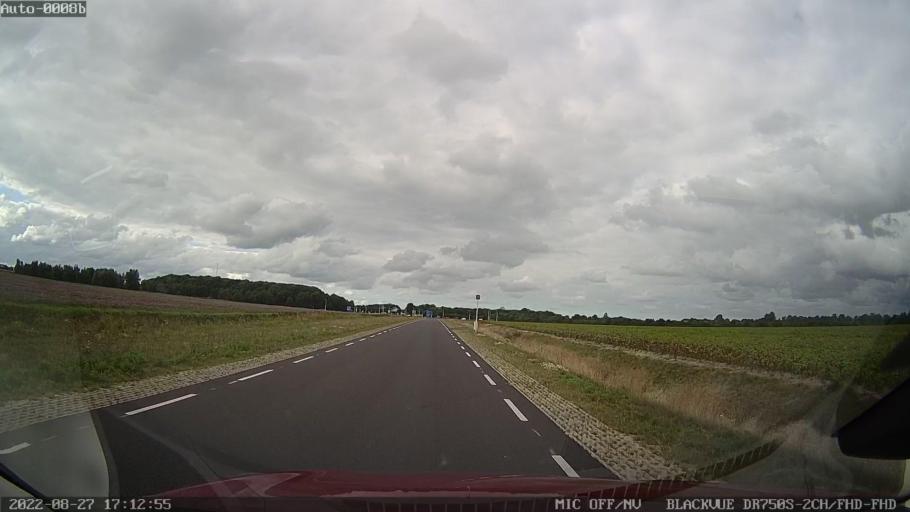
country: NL
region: Zeeland
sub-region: Schouwen-Duiveland
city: Scharendijke
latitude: 51.7305
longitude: 3.8312
